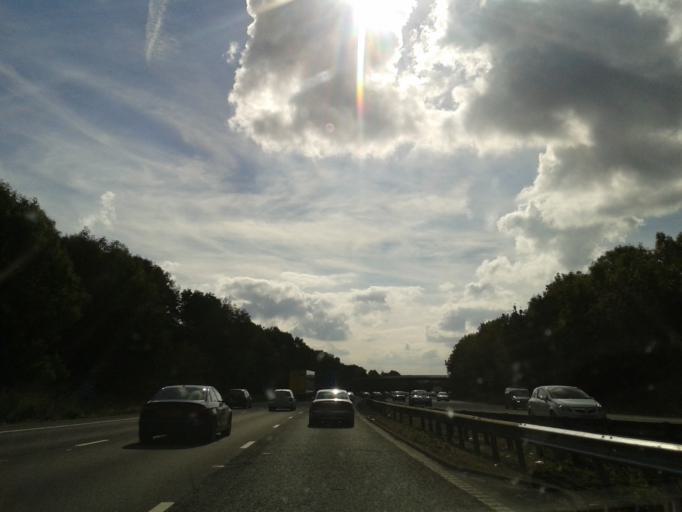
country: GB
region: England
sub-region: Staffordshire
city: Stafford
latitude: 52.8340
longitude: -2.1455
